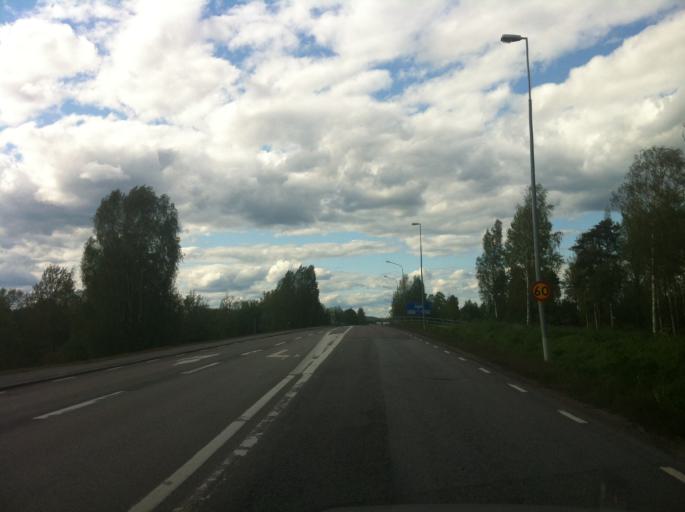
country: SE
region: Vaermland
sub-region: Storfors Kommun
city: Storfors
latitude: 59.5364
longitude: 14.2816
